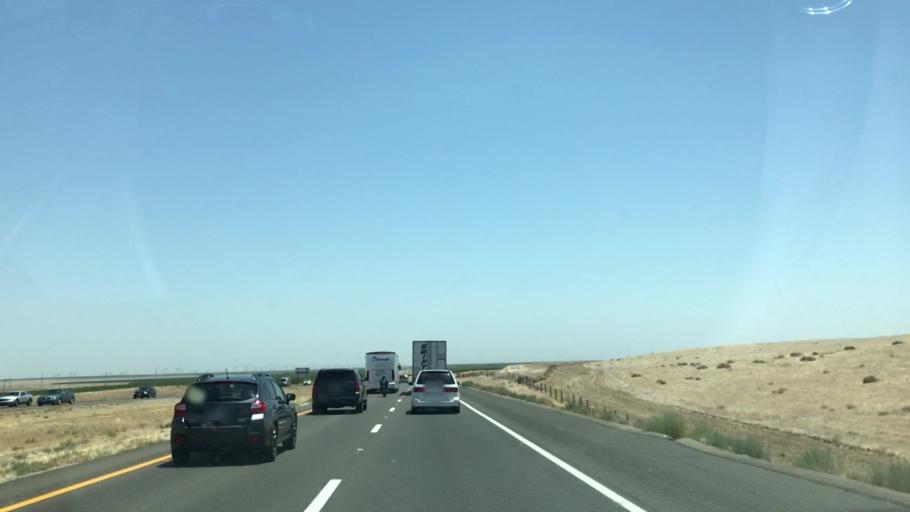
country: US
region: California
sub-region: Kings County
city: Kettleman City
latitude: 35.9658
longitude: -119.9445
